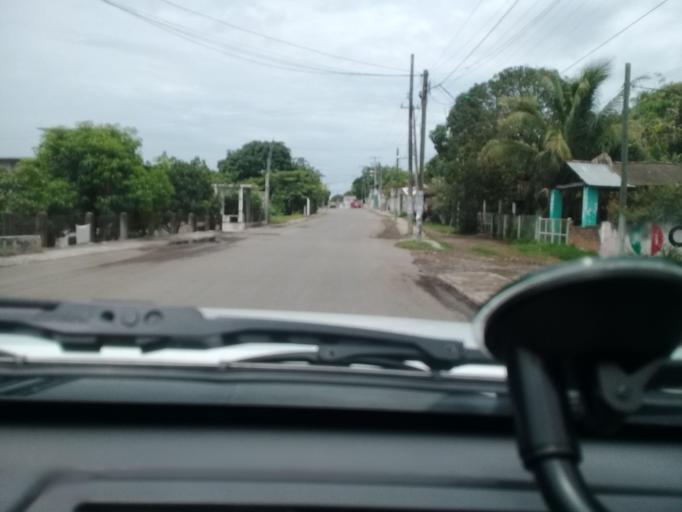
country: MX
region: Veracruz
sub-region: Paso de Ovejas
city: El Hatito
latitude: 19.2797
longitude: -96.3904
